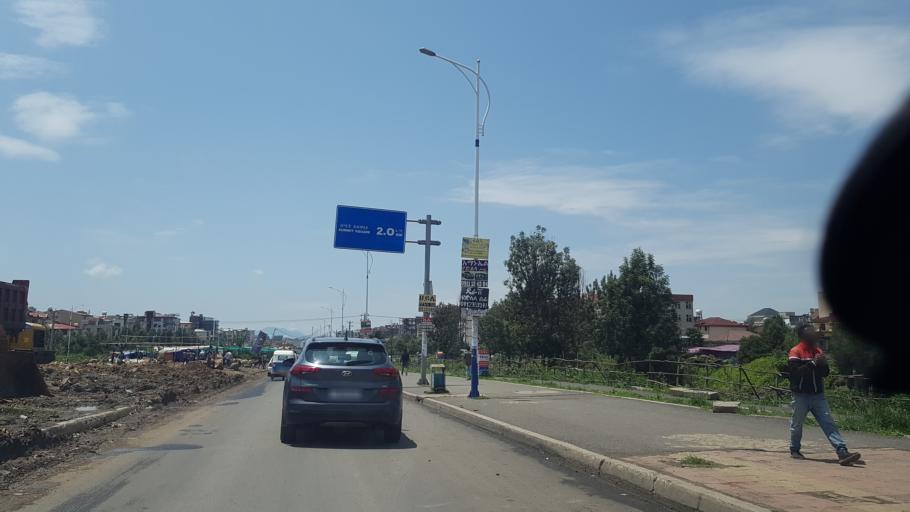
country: ET
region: Adis Abeba
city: Addis Ababa
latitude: 9.0197
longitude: 38.8521
